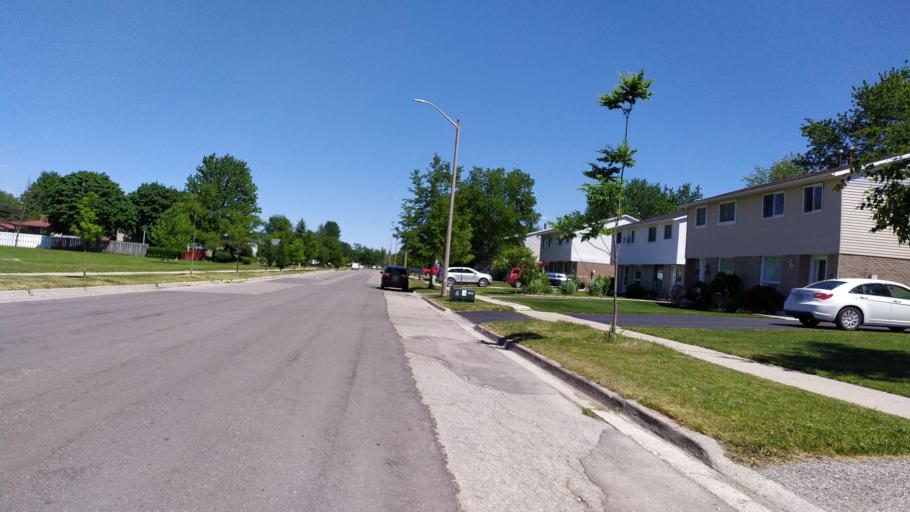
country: CA
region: Ontario
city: Stratford
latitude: 43.3551
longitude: -80.9813
